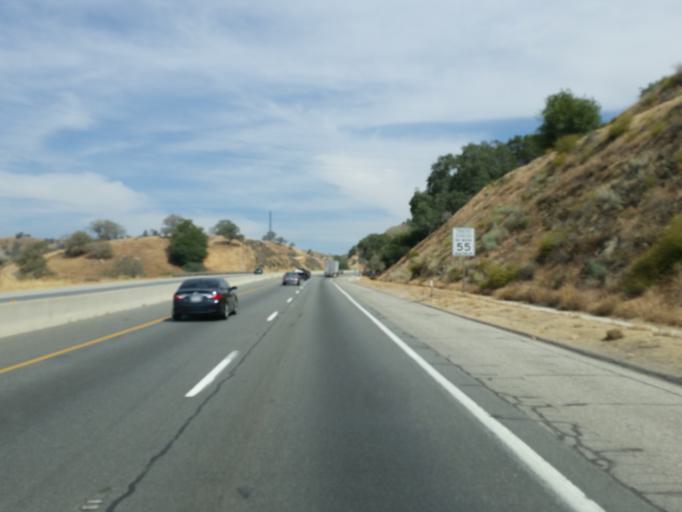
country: US
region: California
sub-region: Kern County
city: Bear Valley Springs
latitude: 35.2597
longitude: -118.6173
